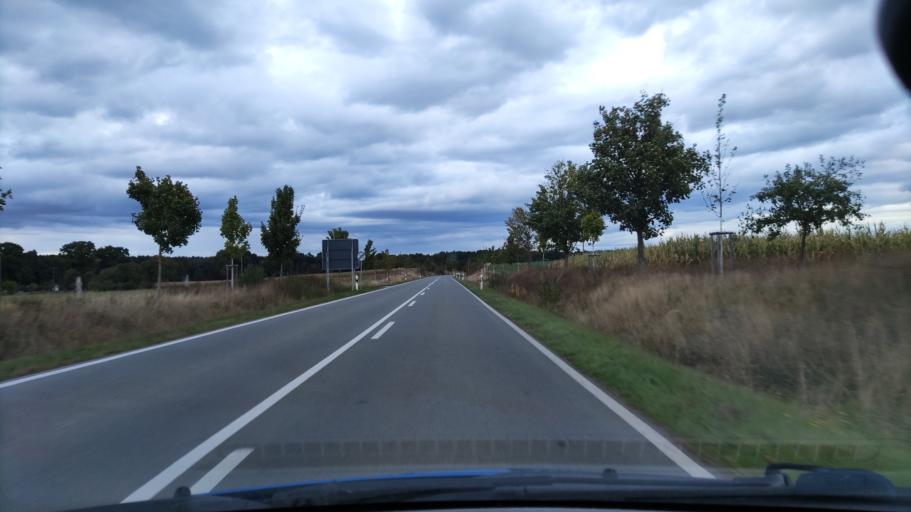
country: DE
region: Mecklenburg-Vorpommern
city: Lubtheen
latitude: 53.3675
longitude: 10.9640
